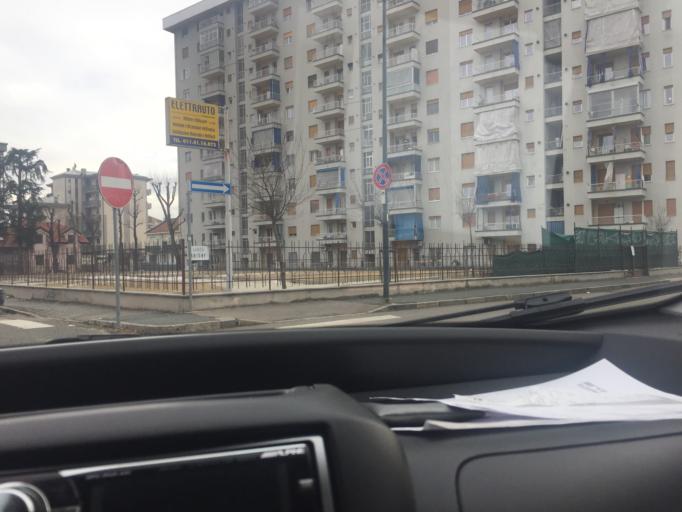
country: IT
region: Piedmont
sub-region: Provincia di Torino
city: Collegno
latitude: 45.0746
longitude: 7.6004
